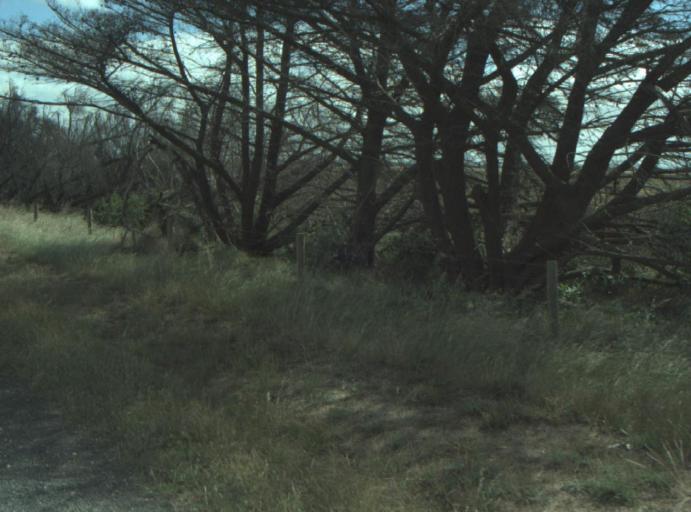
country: AU
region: Victoria
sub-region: Greater Geelong
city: Lara
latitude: -37.8950
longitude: 144.3186
